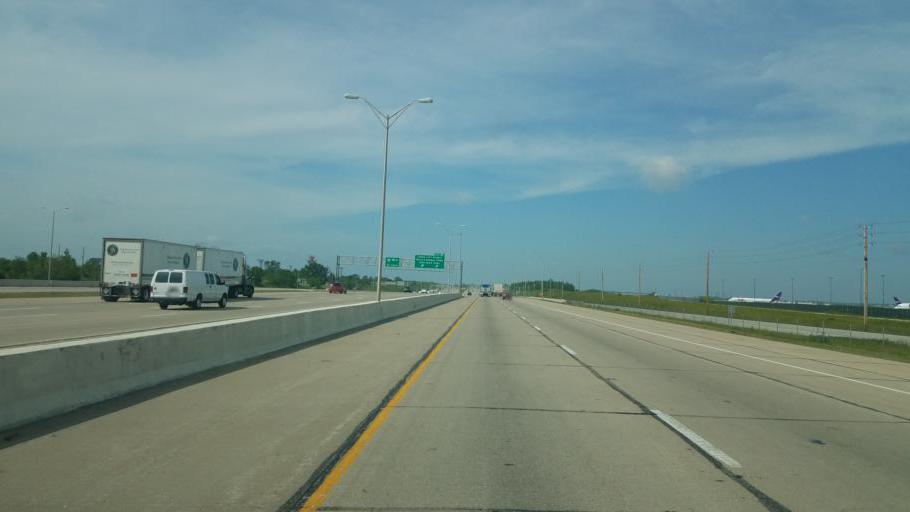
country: US
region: Indiana
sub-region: Marion County
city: Speedway
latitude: 39.7083
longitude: -86.2843
